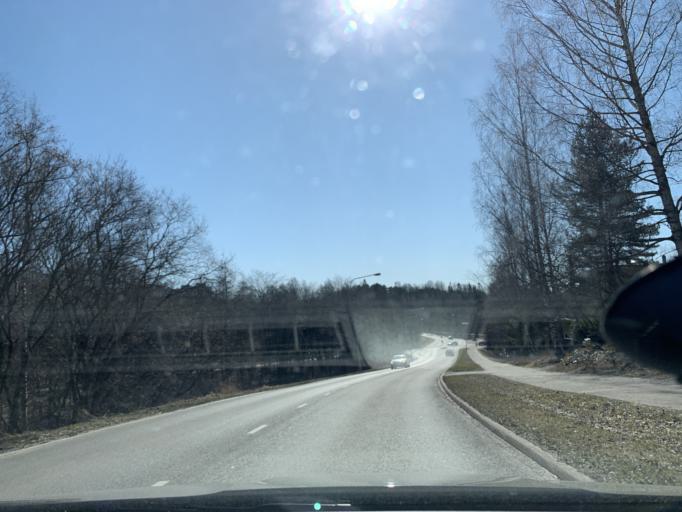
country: FI
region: Uusimaa
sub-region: Helsinki
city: Espoo
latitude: 60.1434
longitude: 24.6565
